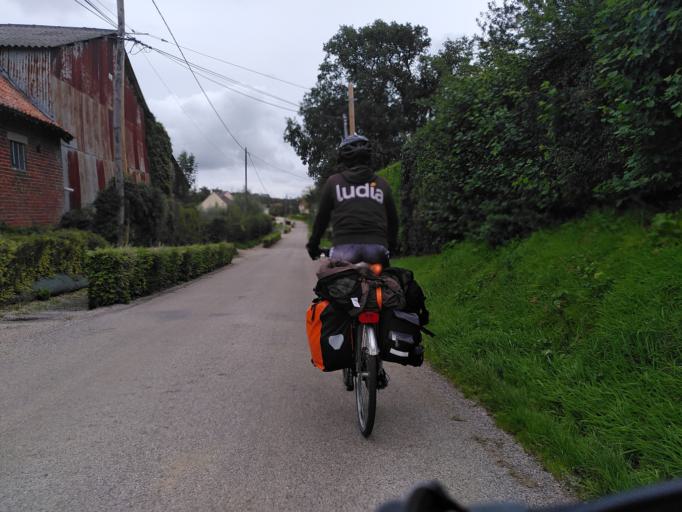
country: FR
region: Nord-Pas-de-Calais
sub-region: Departement du Pas-de-Calais
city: Desvres
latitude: 50.6497
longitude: 1.9407
